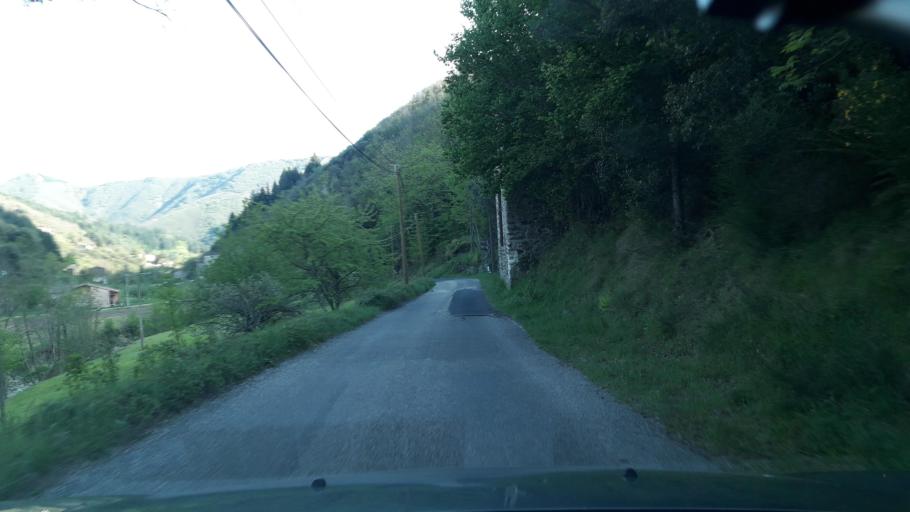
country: FR
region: Languedoc-Roussillon
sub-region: Departement du Gard
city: Valleraugue
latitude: 44.0947
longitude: 3.6344
